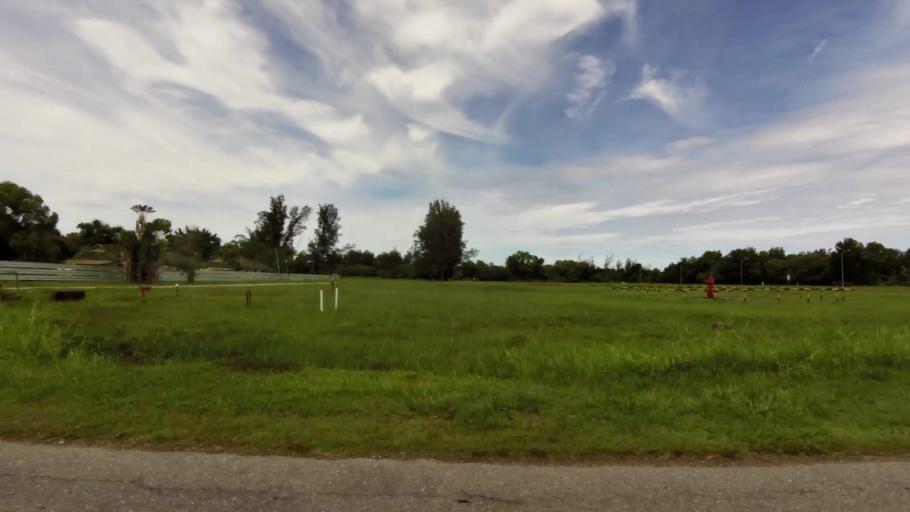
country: BN
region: Belait
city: Seria
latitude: 4.6073
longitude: 114.3081
